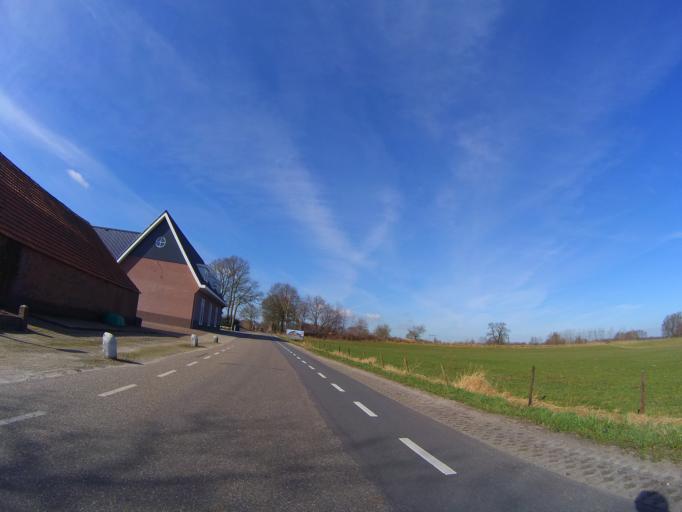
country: NL
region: Utrecht
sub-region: Gemeente Veenendaal
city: Veenendaal
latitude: 52.0476
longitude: 5.5405
